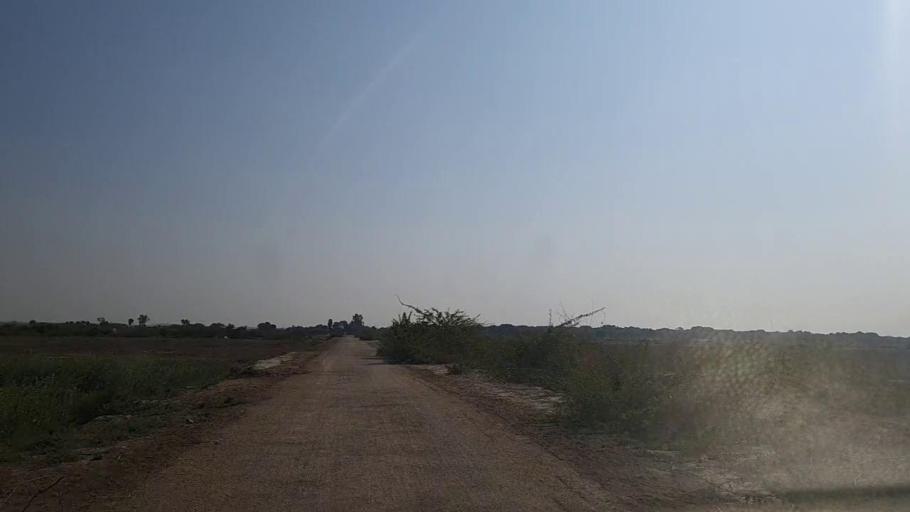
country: PK
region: Sindh
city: Naukot
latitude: 24.8982
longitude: 69.4697
